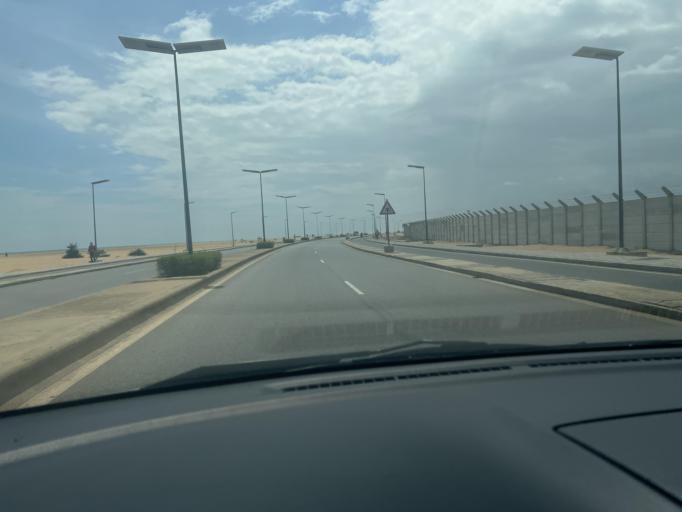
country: BJ
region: Littoral
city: Cotonou
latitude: 6.3486
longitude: 2.3770
